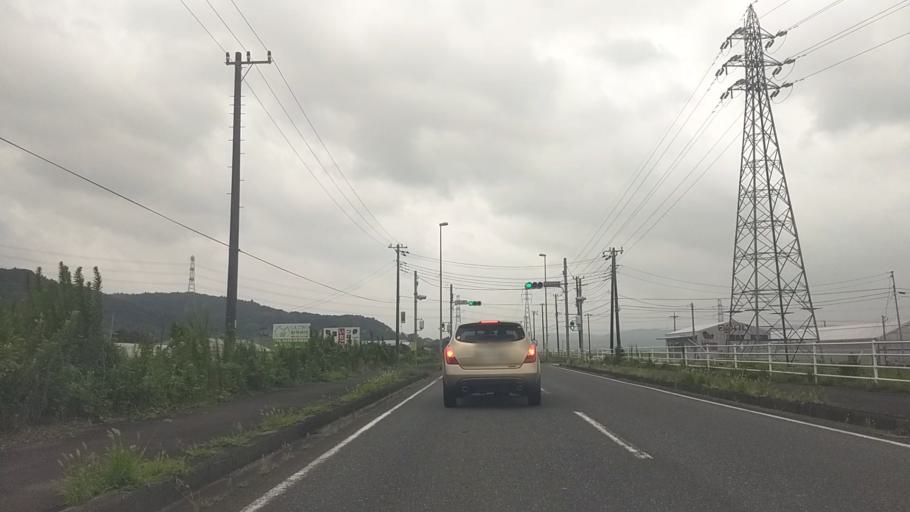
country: JP
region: Chiba
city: Kisarazu
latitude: 35.3511
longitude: 140.0548
